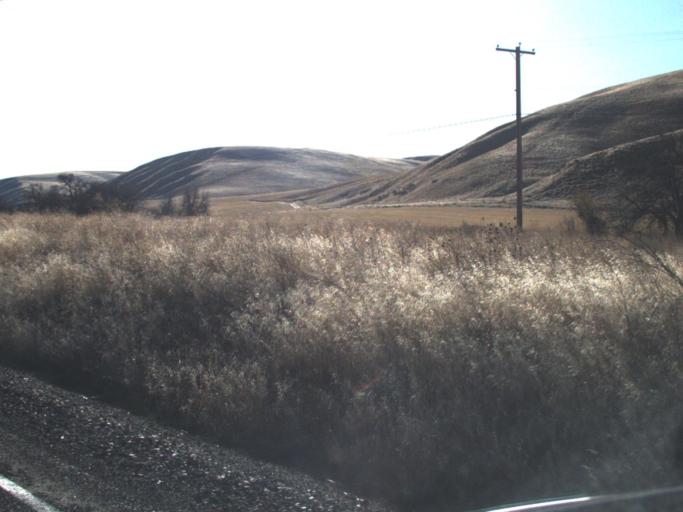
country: US
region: Washington
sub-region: Garfield County
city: Pomeroy
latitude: 46.4832
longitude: -117.7414
